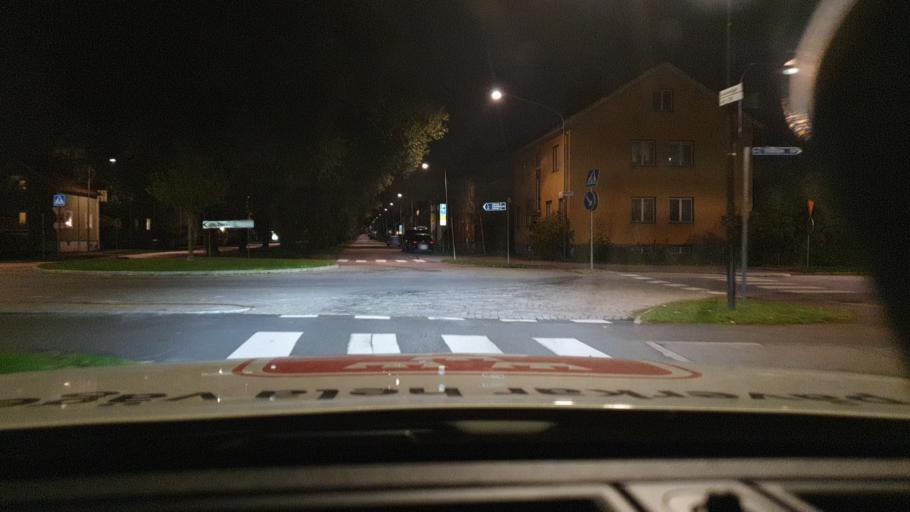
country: SE
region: Stockholm
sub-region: Stockholms Kommun
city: Arsta
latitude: 59.2819
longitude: 18.0776
